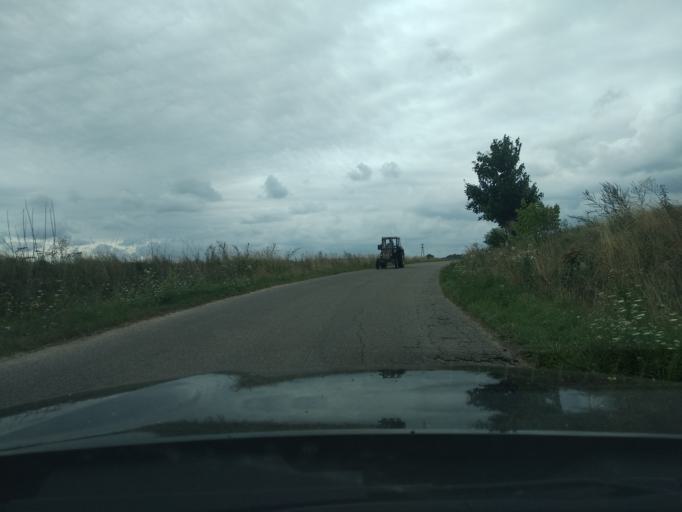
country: PL
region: Masovian Voivodeship
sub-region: Powiat pultuski
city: Obryte
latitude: 52.7543
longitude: 21.2170
